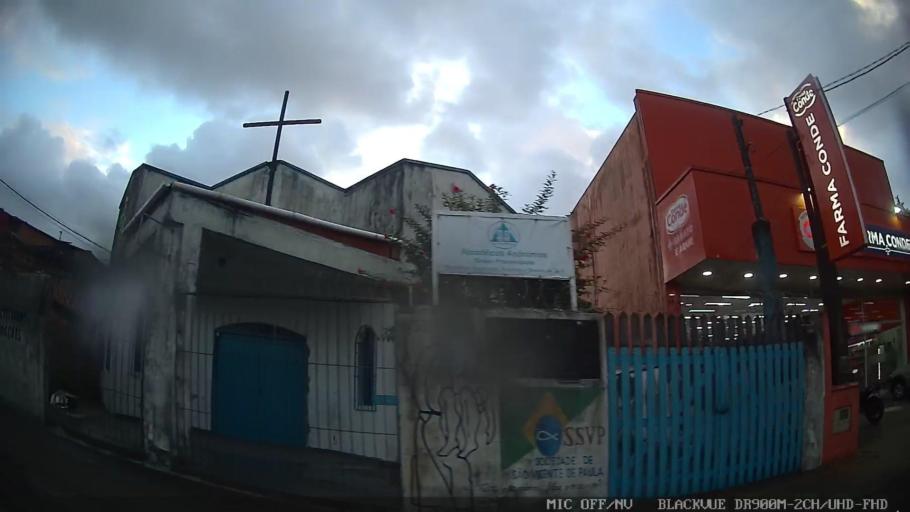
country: BR
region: Sao Paulo
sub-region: Itanhaem
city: Itanhaem
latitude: -24.1698
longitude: -46.7854
